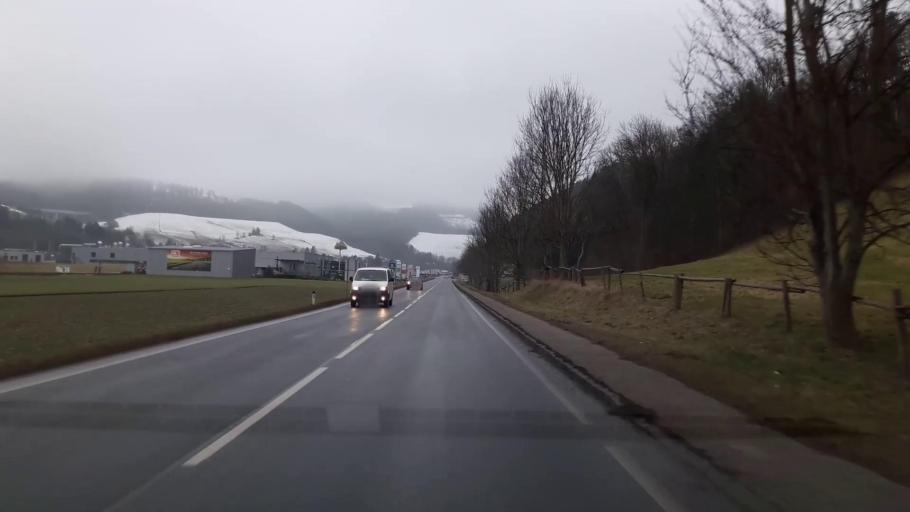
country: AT
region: Lower Austria
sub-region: Politischer Bezirk Neunkirchen
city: Grimmenstein
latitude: 47.6054
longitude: 16.1190
